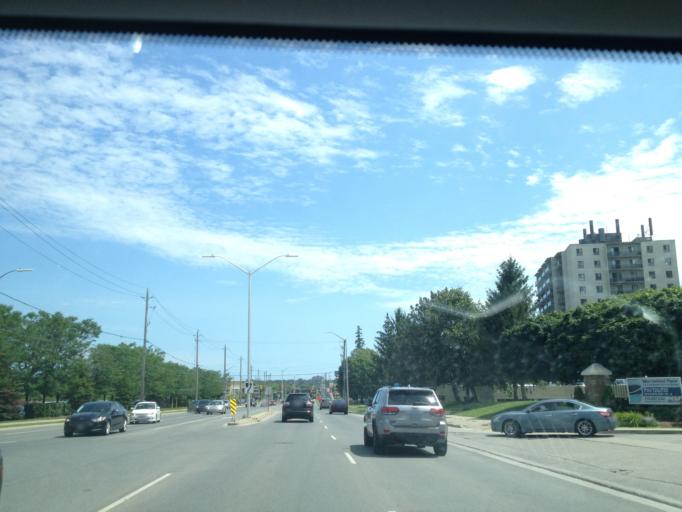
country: CA
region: Ontario
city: London
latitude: 42.9875
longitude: -81.2946
